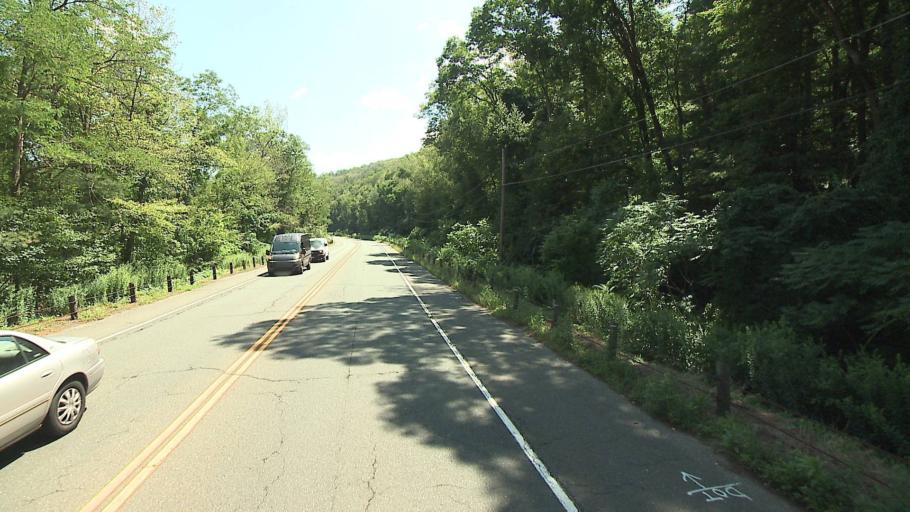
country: US
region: Connecticut
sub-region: Hartford County
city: Collinsville
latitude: 41.7809
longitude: -72.9220
